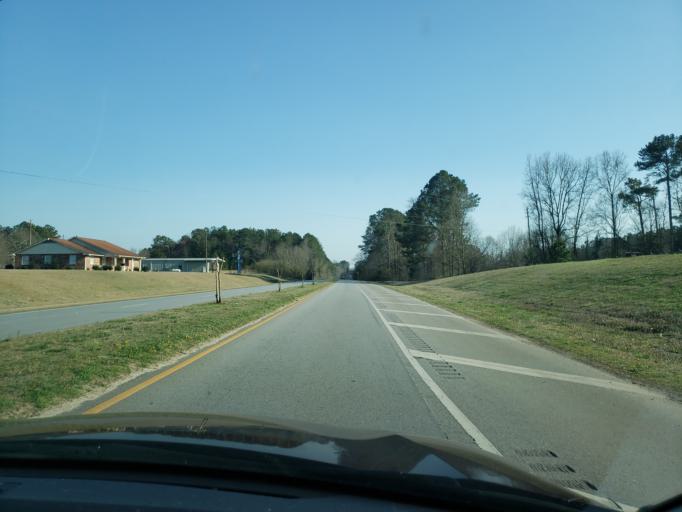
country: US
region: Alabama
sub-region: Randolph County
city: Wedowee
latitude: 33.2899
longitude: -85.4748
